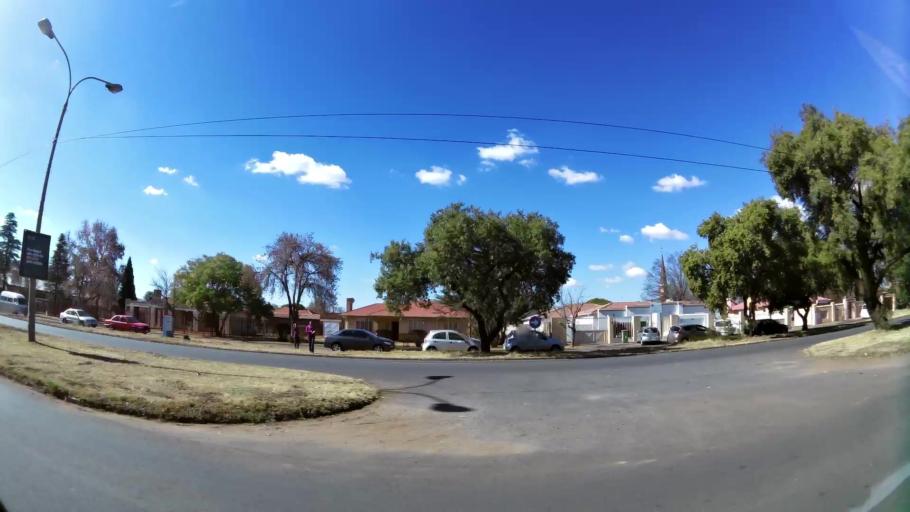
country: ZA
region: Gauteng
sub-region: West Rand District Municipality
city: Carletonville
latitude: -26.3530
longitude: 27.3984
